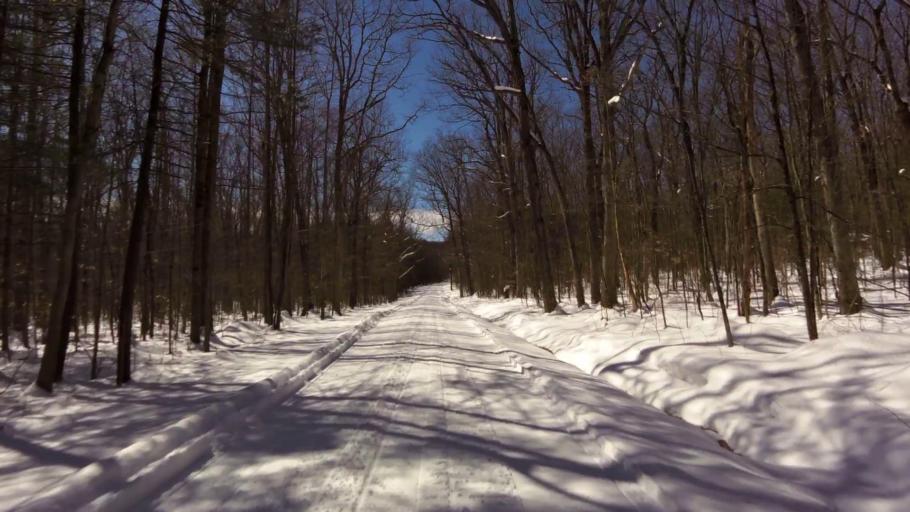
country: US
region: New York
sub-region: Allegany County
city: Houghton
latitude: 42.3492
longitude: -78.1955
